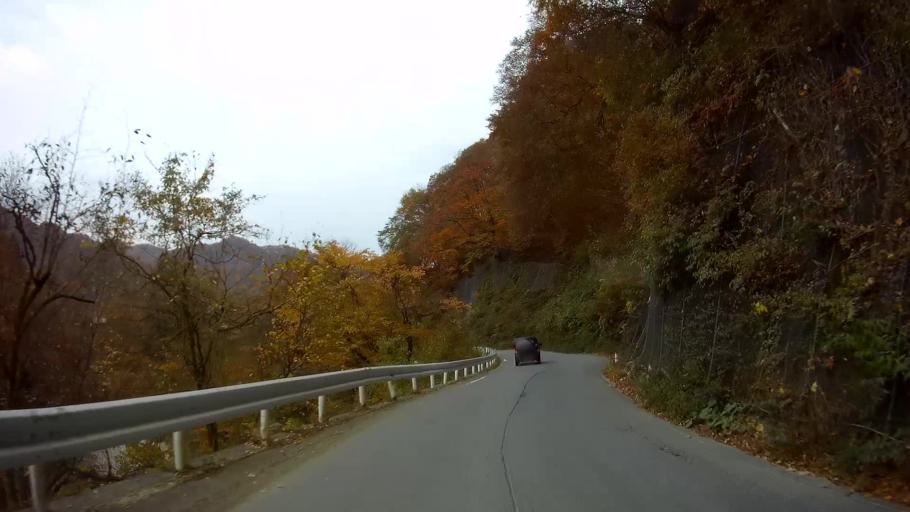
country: JP
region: Gunma
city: Nakanojomachi
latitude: 36.6301
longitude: 138.6502
